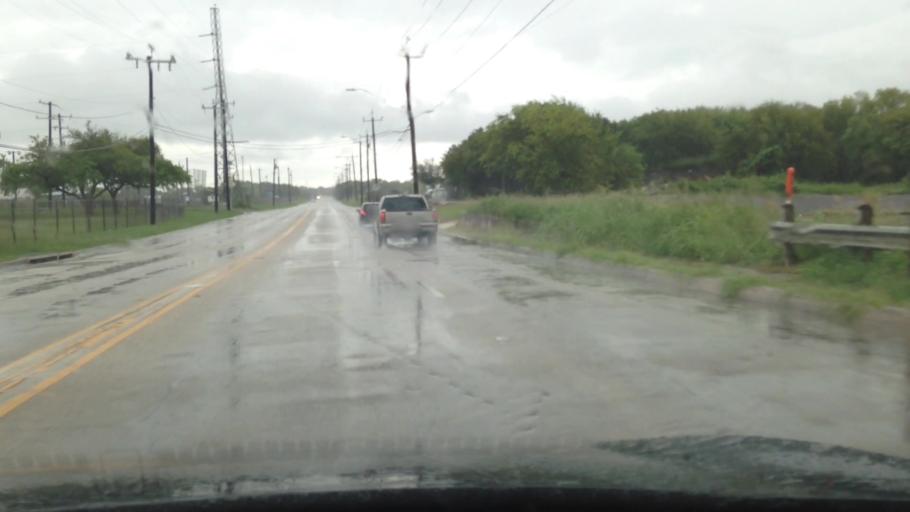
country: US
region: Texas
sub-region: Bexar County
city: Windcrest
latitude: 29.5447
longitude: -98.4173
